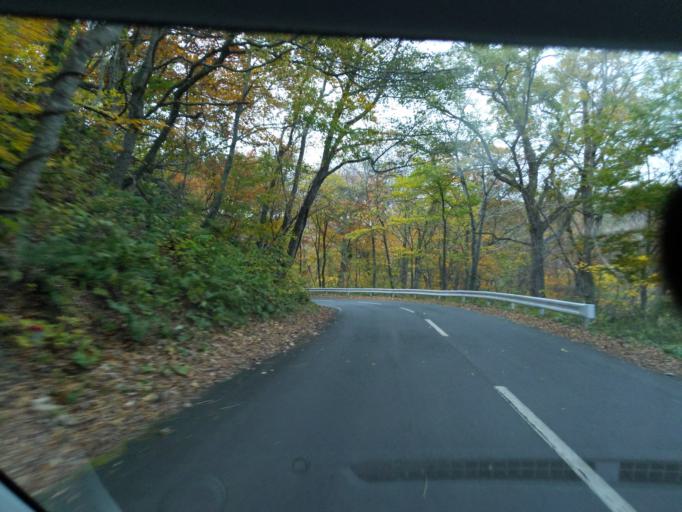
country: JP
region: Iwate
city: Mizusawa
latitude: 39.1048
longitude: 140.8633
